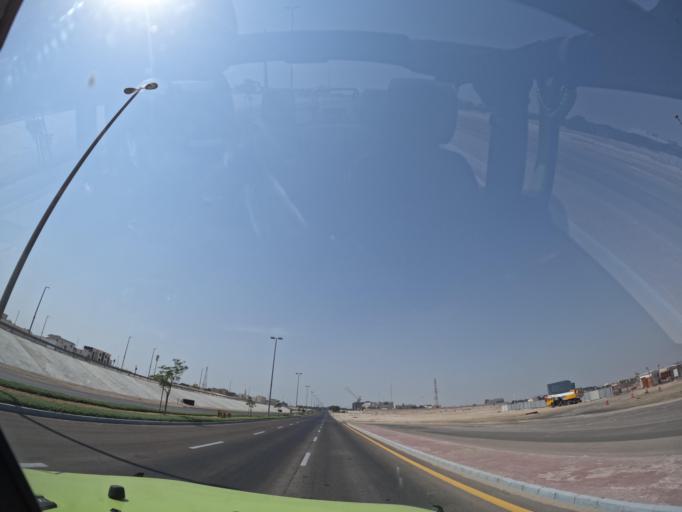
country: AE
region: Abu Dhabi
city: Abu Dhabi
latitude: 24.3097
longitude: 54.6154
